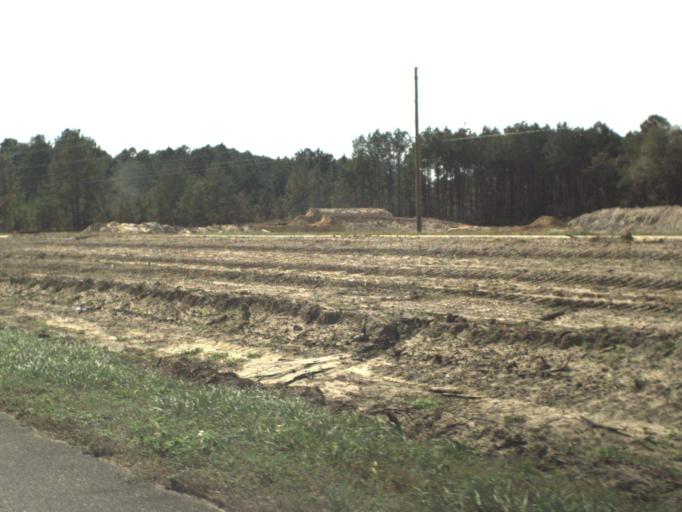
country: US
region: Florida
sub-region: Holmes County
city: Bonifay
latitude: 30.6454
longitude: -85.7002
